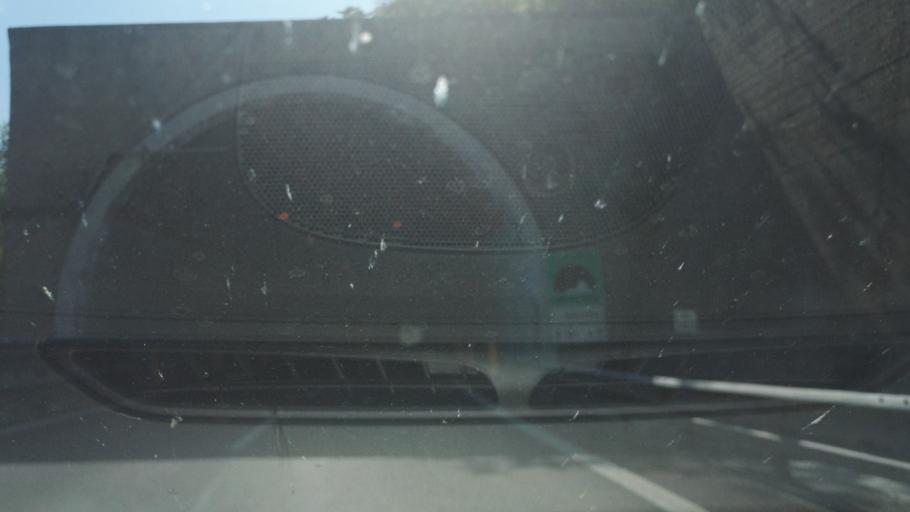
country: IT
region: Calabria
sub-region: Provincia di Cosenza
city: Altilia
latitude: 39.1260
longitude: 16.2632
